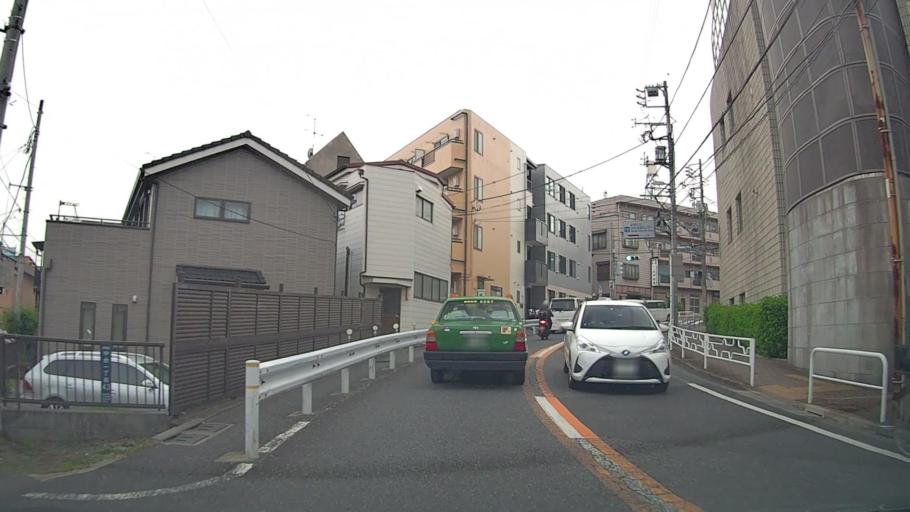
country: JP
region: Saitama
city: Shimotoda
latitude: 35.7674
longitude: 139.6768
